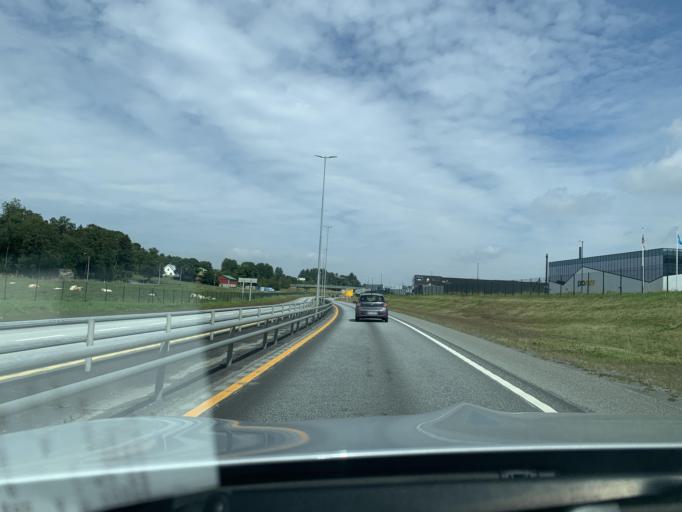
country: NO
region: Rogaland
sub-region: Sola
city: Sola
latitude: 58.8981
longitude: 5.6809
